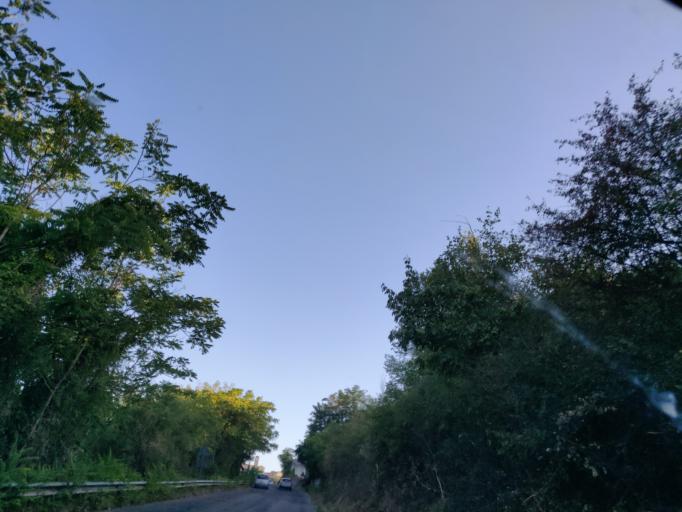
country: IT
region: Latium
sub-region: Provincia di Viterbo
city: Acquapendente
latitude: 42.7562
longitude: 11.8655
